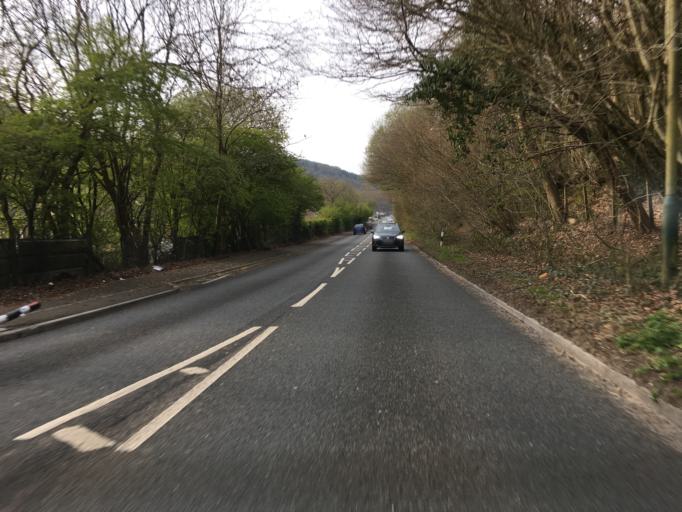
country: GB
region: Wales
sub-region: Caerphilly County Borough
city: Bedwas
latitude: 51.6239
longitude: -3.1841
